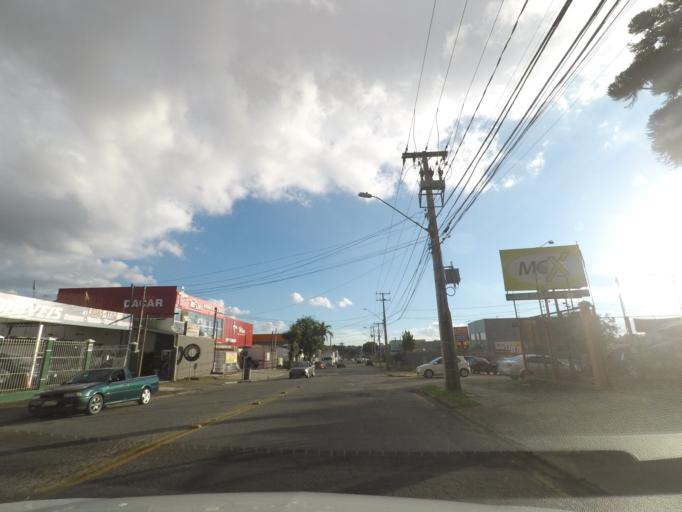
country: BR
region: Parana
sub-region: Sao Jose Dos Pinhais
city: Sao Jose dos Pinhais
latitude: -25.5016
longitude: -49.2551
